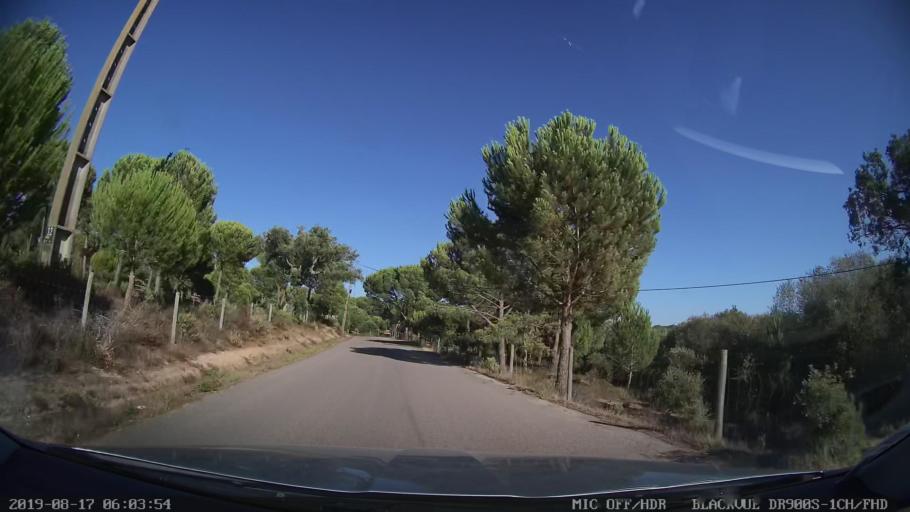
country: PT
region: Santarem
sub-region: Benavente
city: Poceirao
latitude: 38.8465
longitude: -8.7099
